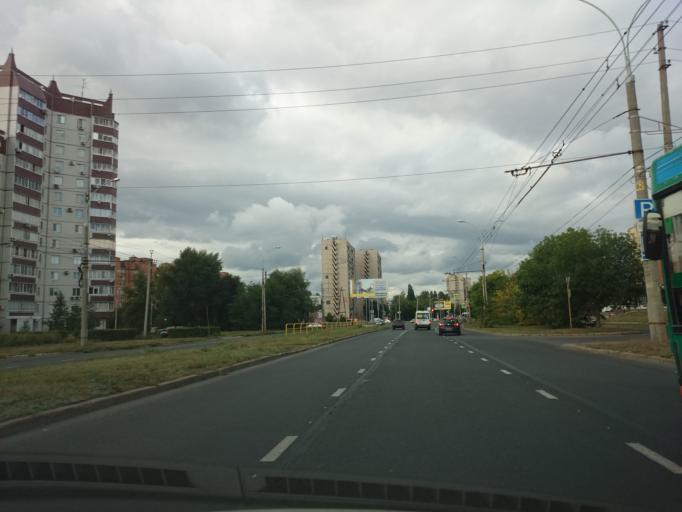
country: RU
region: Samara
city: Tol'yatti
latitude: 53.5034
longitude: 49.2995
